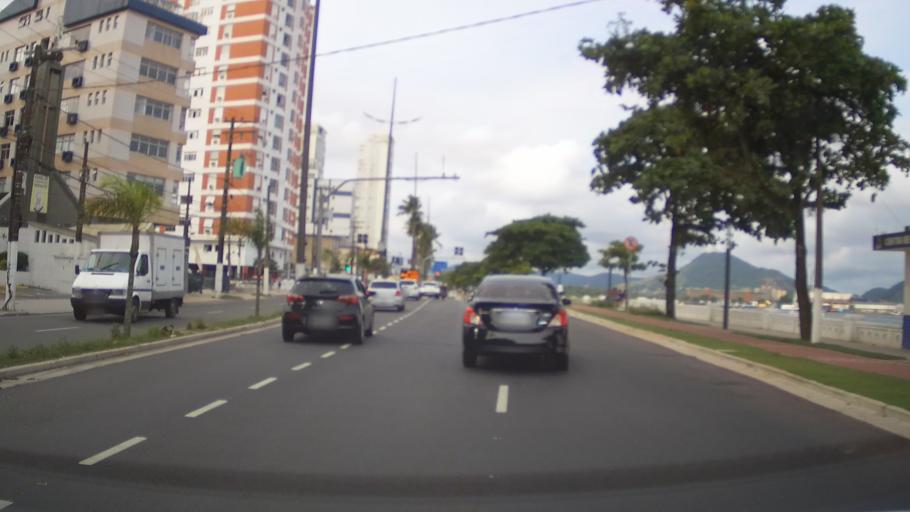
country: BR
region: Sao Paulo
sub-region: Guaruja
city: Guaruja
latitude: -23.9905
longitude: -46.2993
